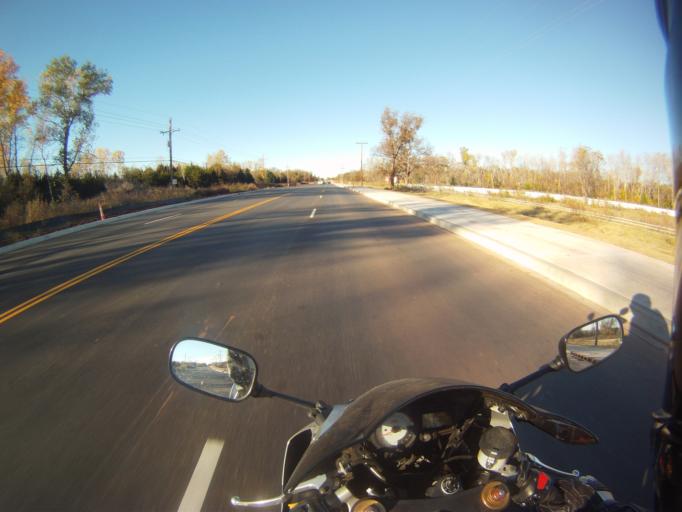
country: US
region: Oklahoma
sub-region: Payne County
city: Stillwater
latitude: 36.1196
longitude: -97.1228
